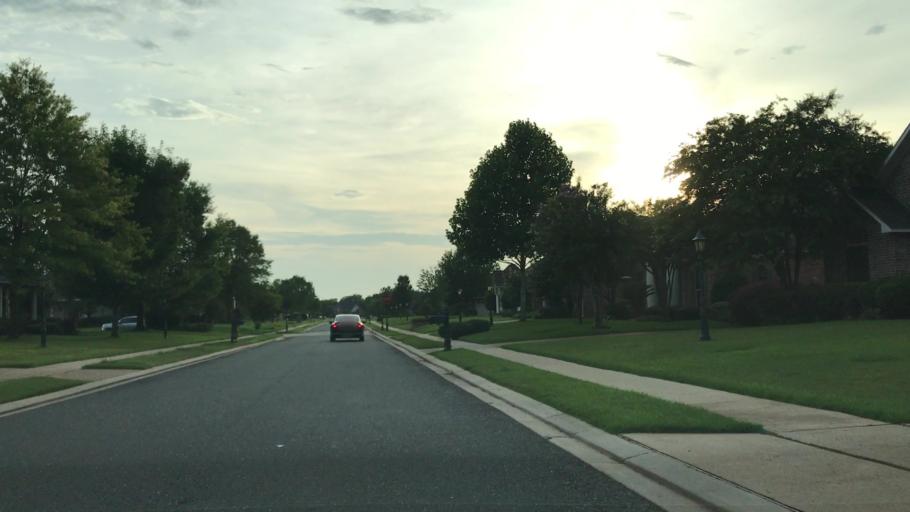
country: US
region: Louisiana
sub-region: Bossier Parish
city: Bossier City
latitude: 32.4187
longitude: -93.7100
